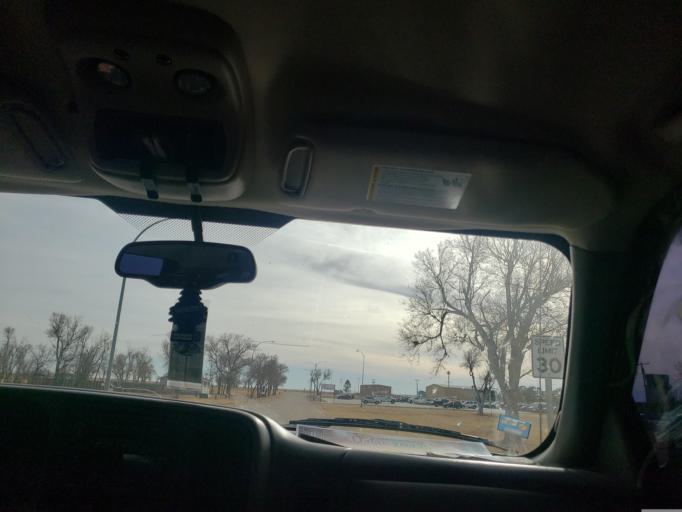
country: US
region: Kansas
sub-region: Finney County
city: Garden City
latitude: 37.9287
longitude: -100.7181
